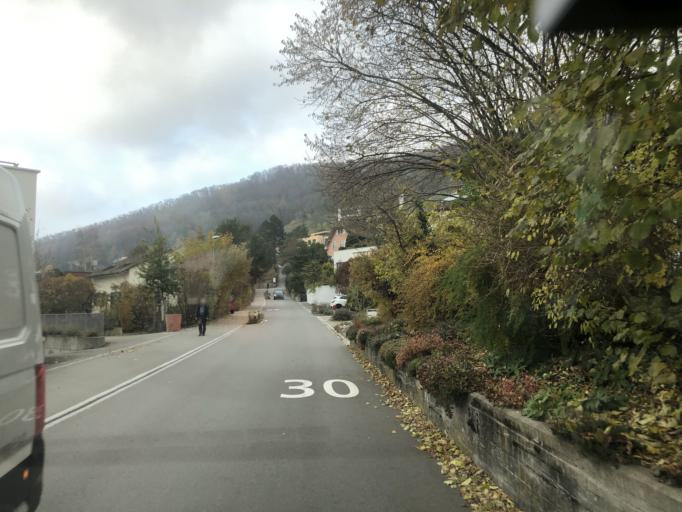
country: CH
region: Aargau
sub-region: Bezirk Baden
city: Wettingen
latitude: 47.4694
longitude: 8.3302
